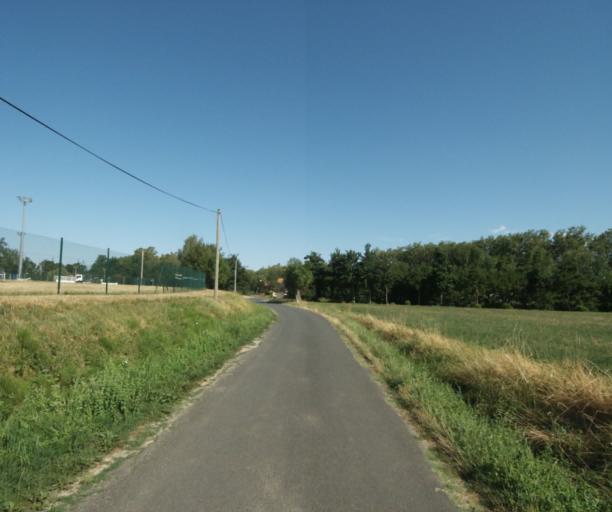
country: FR
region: Midi-Pyrenees
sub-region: Departement de la Haute-Garonne
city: Revel
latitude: 43.4526
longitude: 2.0181
